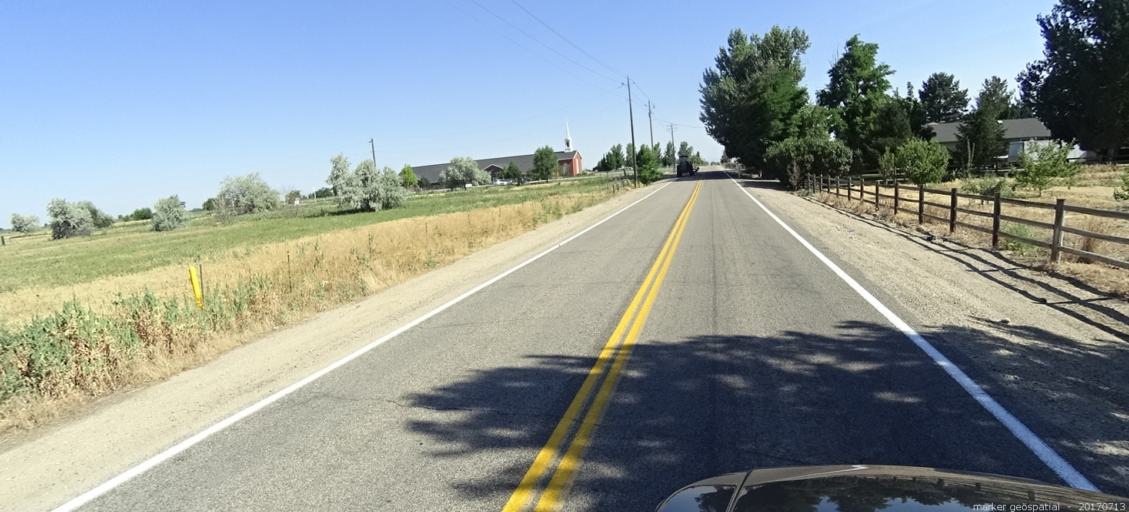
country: US
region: Idaho
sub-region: Ada County
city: Kuna
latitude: 43.5242
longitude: -116.4138
